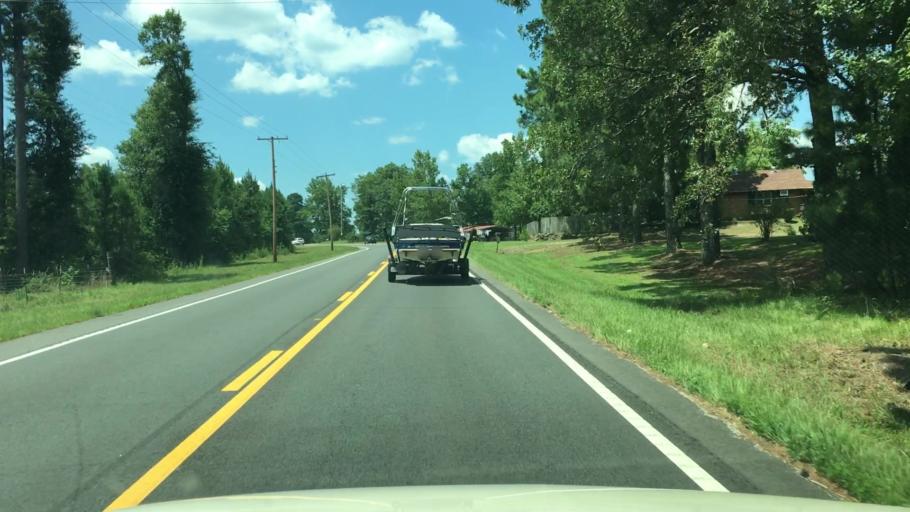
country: US
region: Arkansas
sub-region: Garland County
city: Lake Hamilton
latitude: 34.2760
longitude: -93.1505
